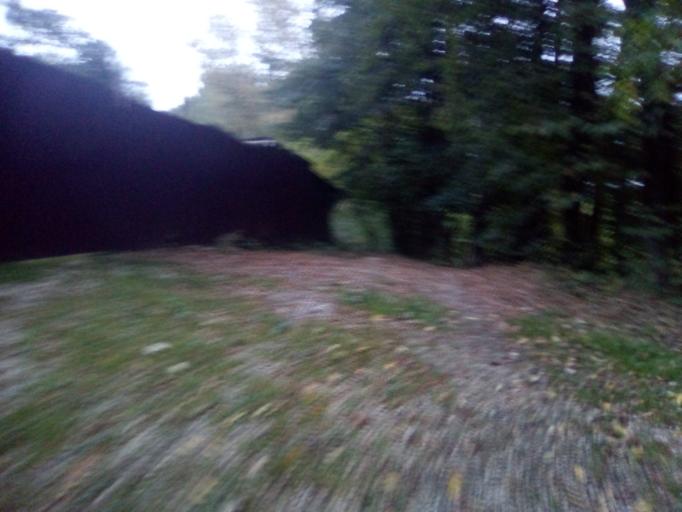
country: RU
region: Moscow
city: Solntsevo
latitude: 55.6568
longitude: 37.3648
